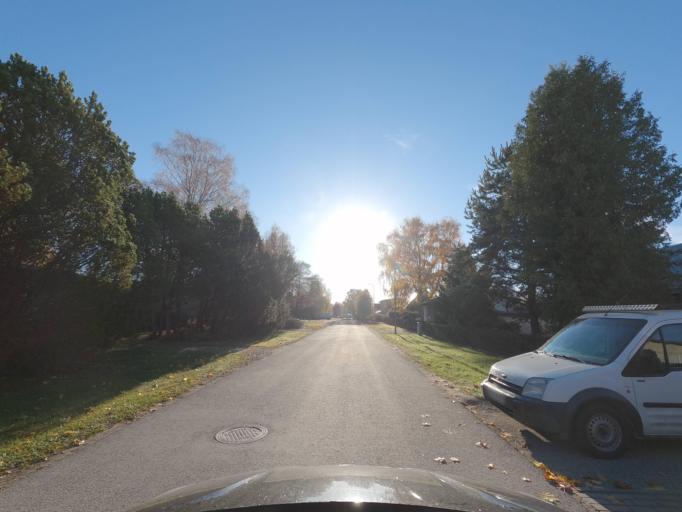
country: EE
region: Raplamaa
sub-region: Kohila vald
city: Kohila
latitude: 59.1667
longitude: 24.7627
